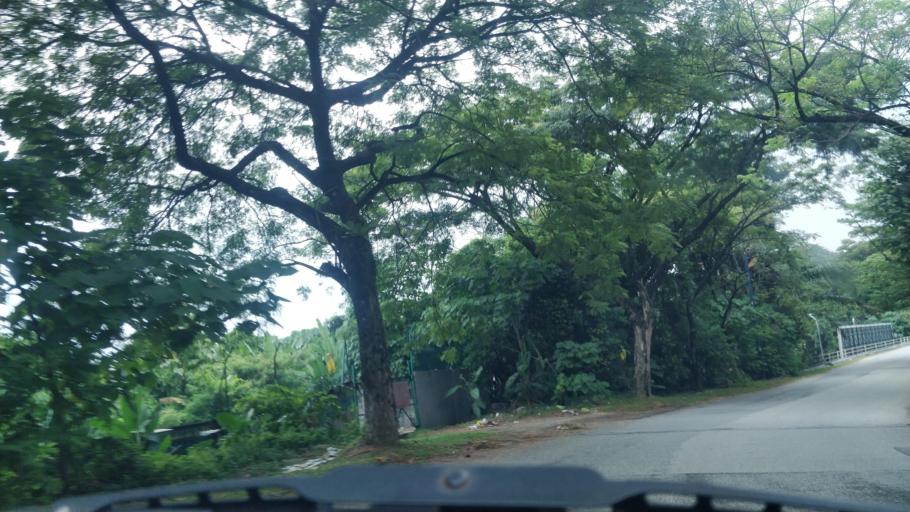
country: MY
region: Selangor
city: Kuang
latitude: 3.2074
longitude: 101.5837
